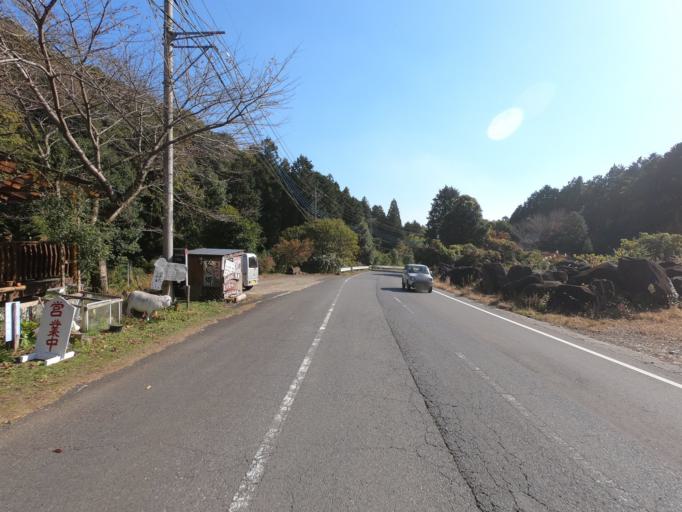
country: JP
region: Ibaraki
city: Makabe
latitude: 36.2352
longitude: 140.1329
